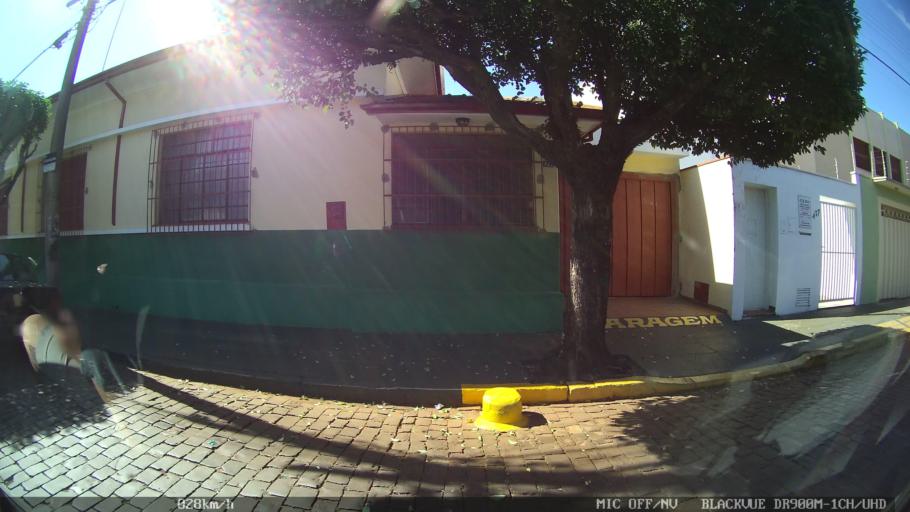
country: BR
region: Sao Paulo
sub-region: Batatais
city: Batatais
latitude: -20.8926
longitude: -47.5834
